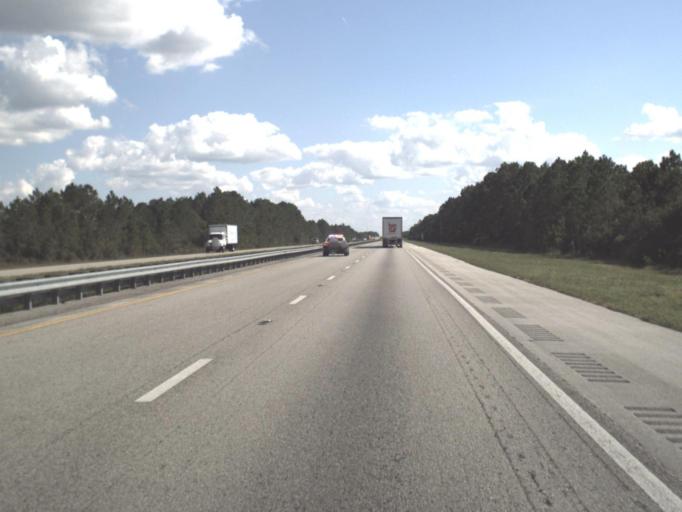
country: US
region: Florida
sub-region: Osceola County
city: Saint Cloud
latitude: 27.9207
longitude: -81.0587
